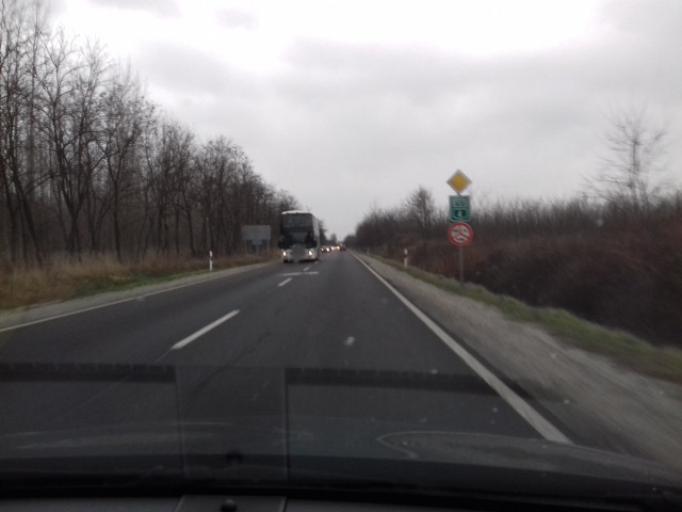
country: HU
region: Szabolcs-Szatmar-Bereg
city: Nyirbogdany
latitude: 48.0393
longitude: 21.8612
